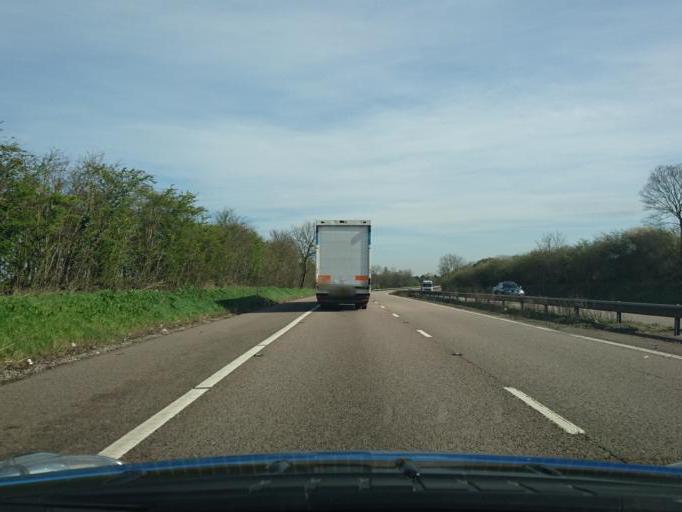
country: GB
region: England
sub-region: Worcestershire
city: Upton upon Severn
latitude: 52.0123
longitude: -2.2370
